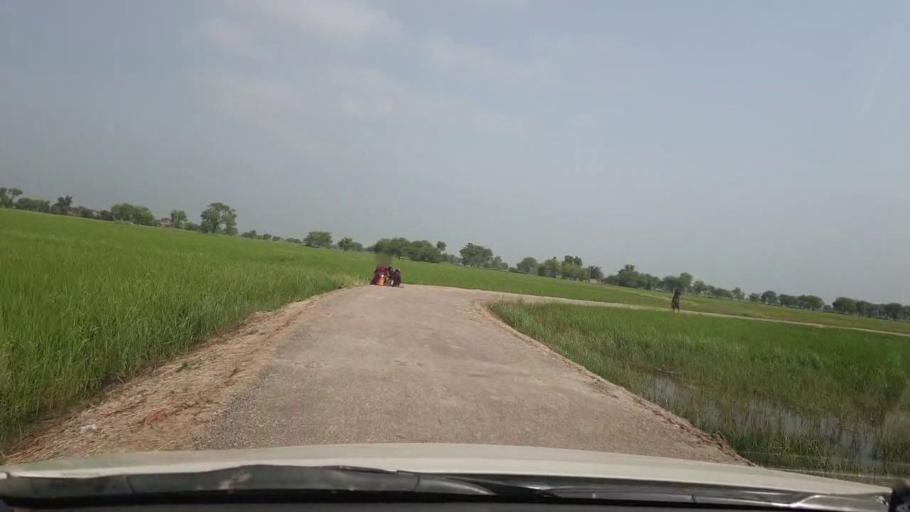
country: PK
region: Sindh
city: Shikarpur
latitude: 27.9922
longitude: 68.6066
